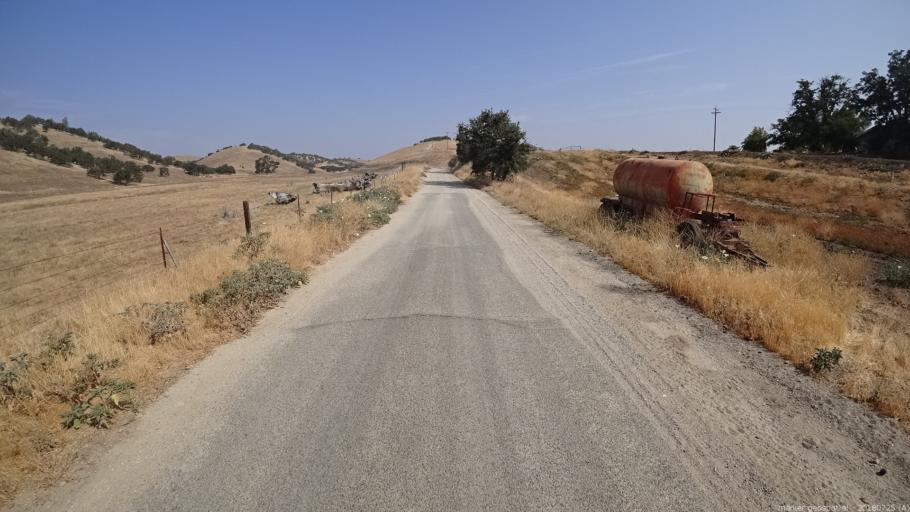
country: US
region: California
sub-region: San Luis Obispo County
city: San Miguel
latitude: 35.8360
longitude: -120.6555
